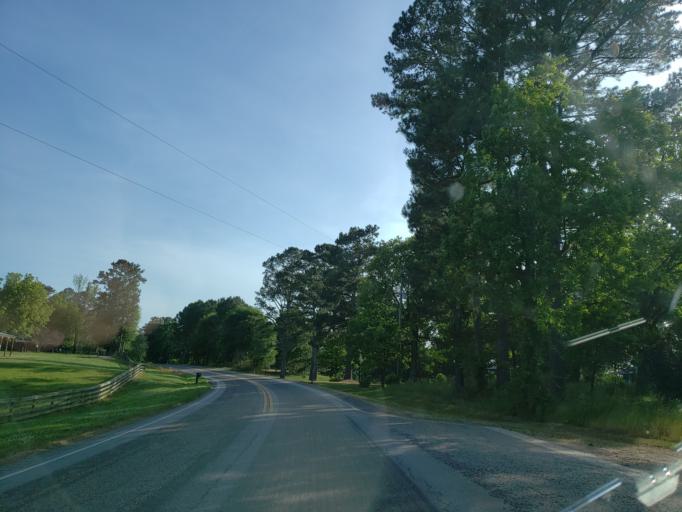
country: US
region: Georgia
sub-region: Carroll County
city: Bowdon
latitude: 33.4647
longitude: -85.3102
